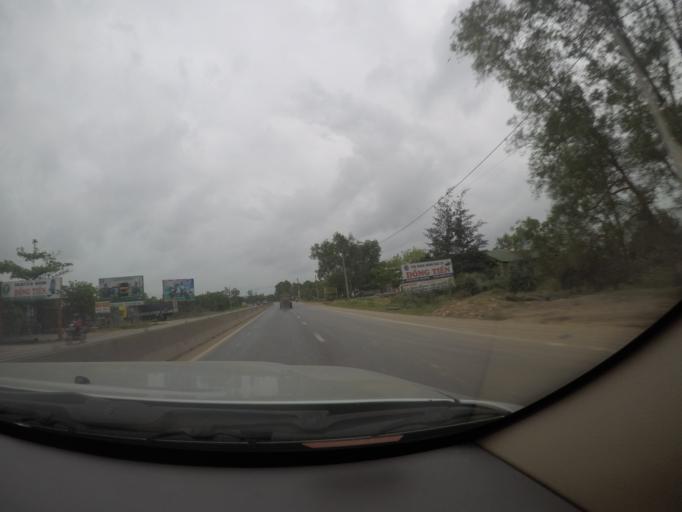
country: VN
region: Quang Tri
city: Ai Tu
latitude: 16.7277
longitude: 107.2030
